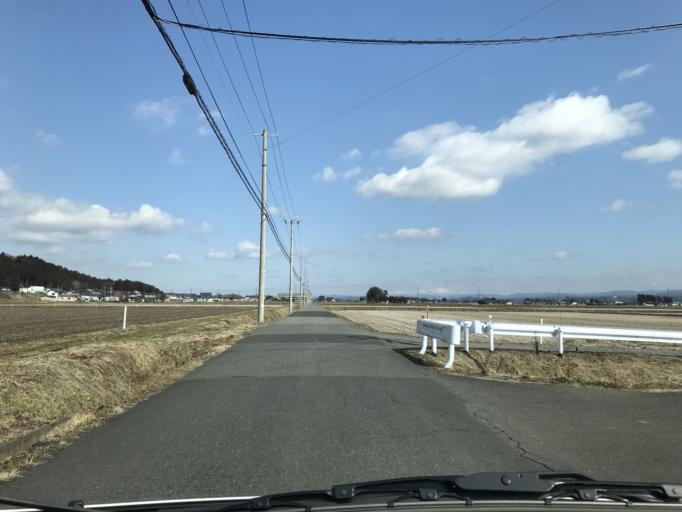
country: JP
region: Iwate
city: Mizusawa
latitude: 39.0709
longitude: 141.1355
